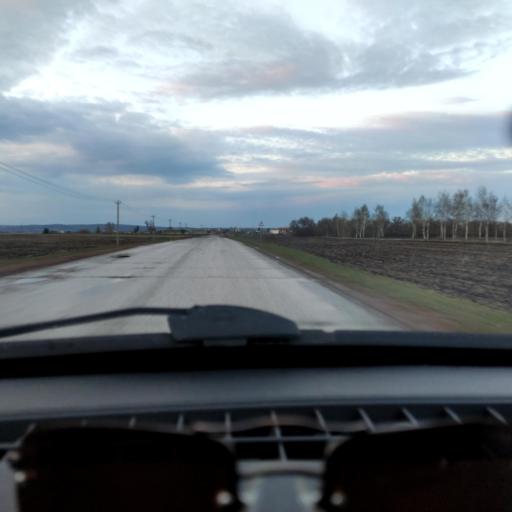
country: RU
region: Bashkortostan
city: Kabakovo
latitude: 54.5445
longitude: 56.0822
